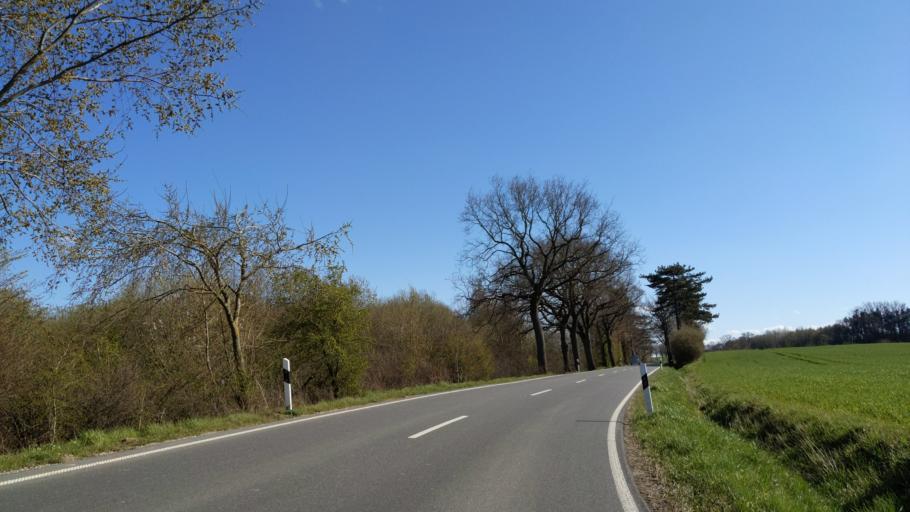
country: DE
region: Schleswig-Holstein
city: Eutin
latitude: 54.0873
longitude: 10.6196
